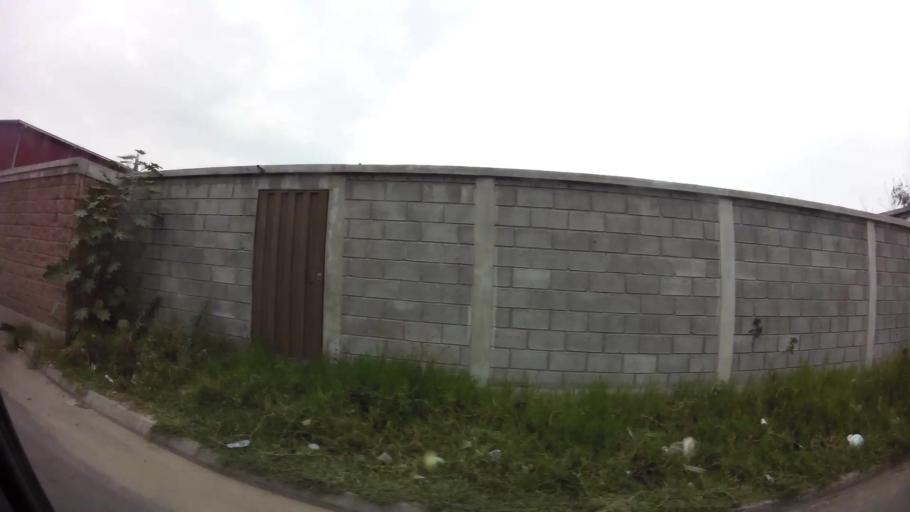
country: HN
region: Francisco Morazan
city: Yaguacire
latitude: 14.0412
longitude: -87.2235
